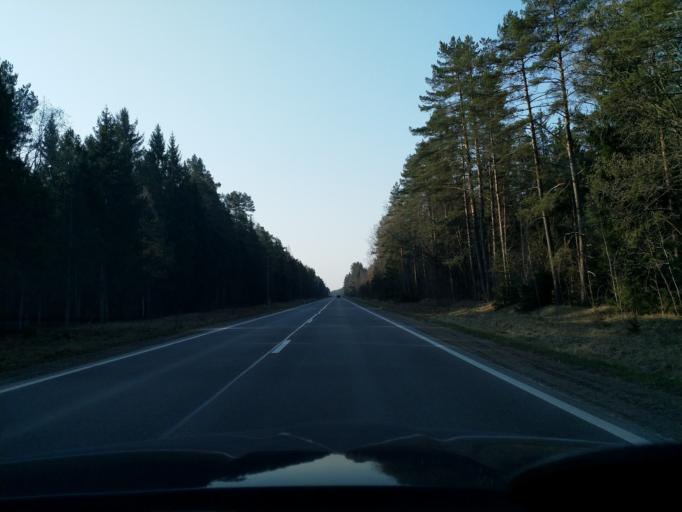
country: LV
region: Rucavas
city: Rucava
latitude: 56.2069
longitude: 21.1347
